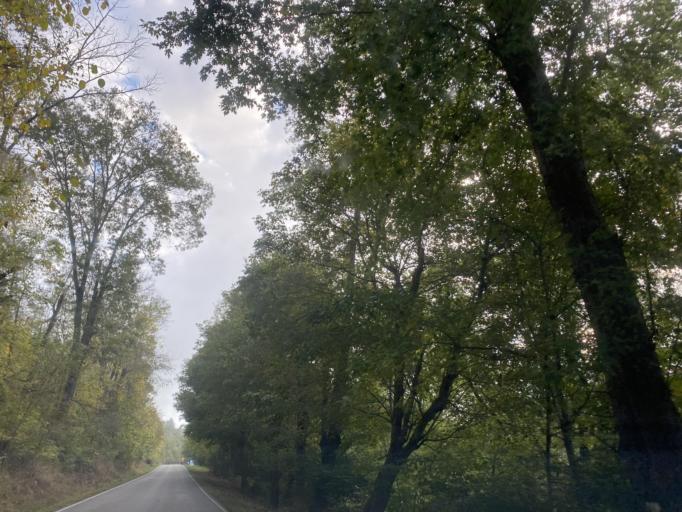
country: US
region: Kentucky
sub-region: Pendleton County
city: Falmouth
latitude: 38.7496
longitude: -84.3335
